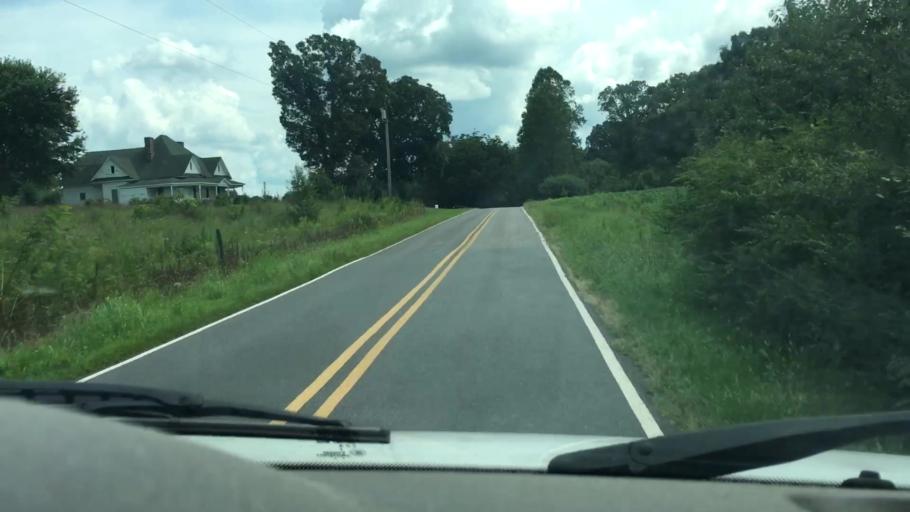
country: US
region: North Carolina
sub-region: Iredell County
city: Troutman
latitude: 35.6703
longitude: -80.8353
